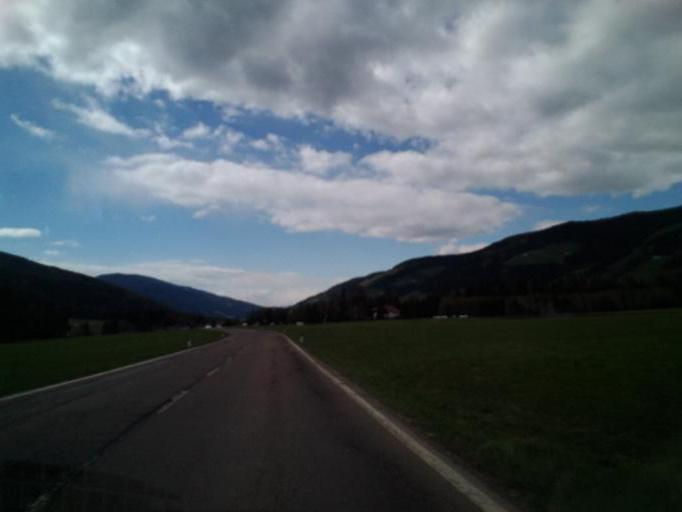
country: IT
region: Trentino-Alto Adige
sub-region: Bolzano
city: Dobbiaco
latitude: 46.7300
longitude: 12.2140
